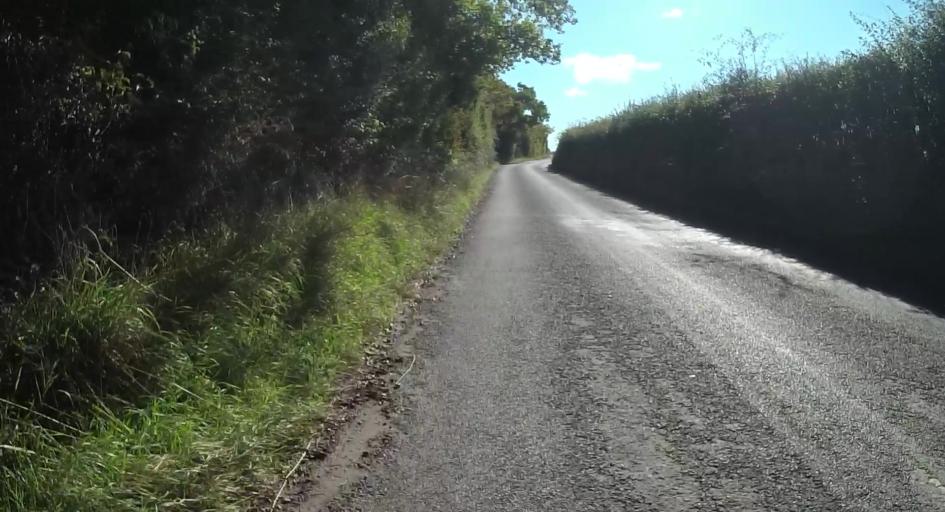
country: GB
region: England
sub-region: Hampshire
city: Hook
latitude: 51.2568
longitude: -0.9878
